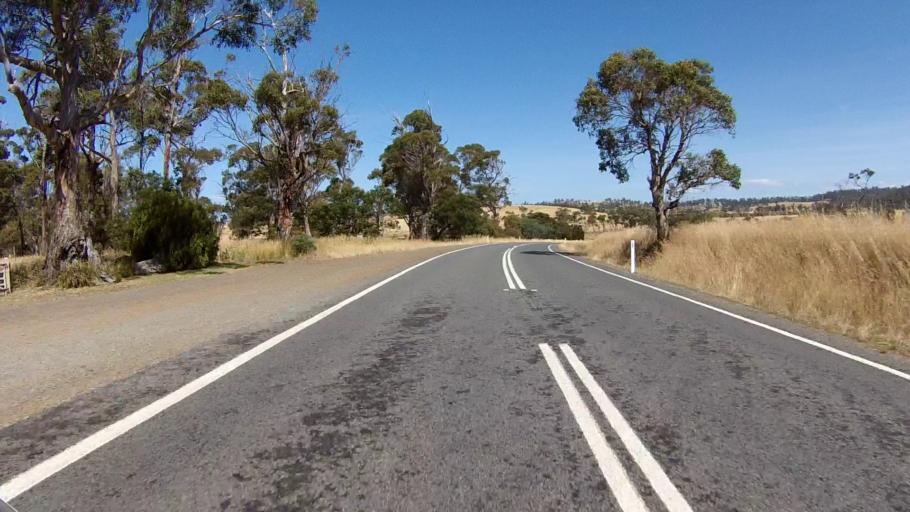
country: AU
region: Tasmania
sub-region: Sorell
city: Sorell
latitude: -42.4520
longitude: 147.9302
